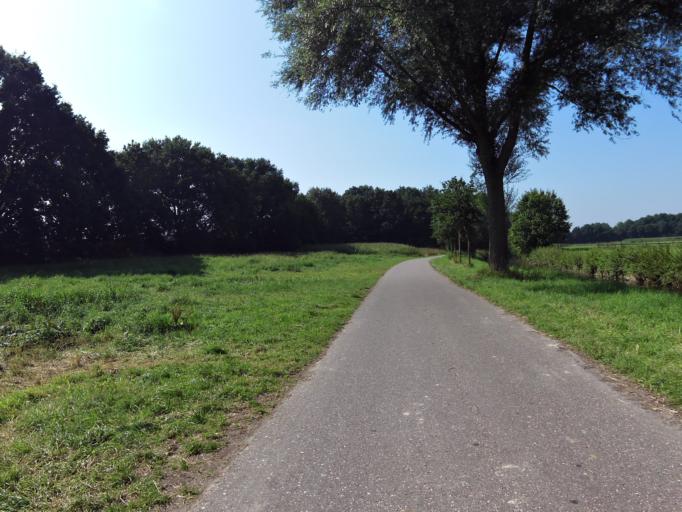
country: DE
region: North Rhine-Westphalia
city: Geilenkirchen
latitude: 50.9939
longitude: 6.1707
